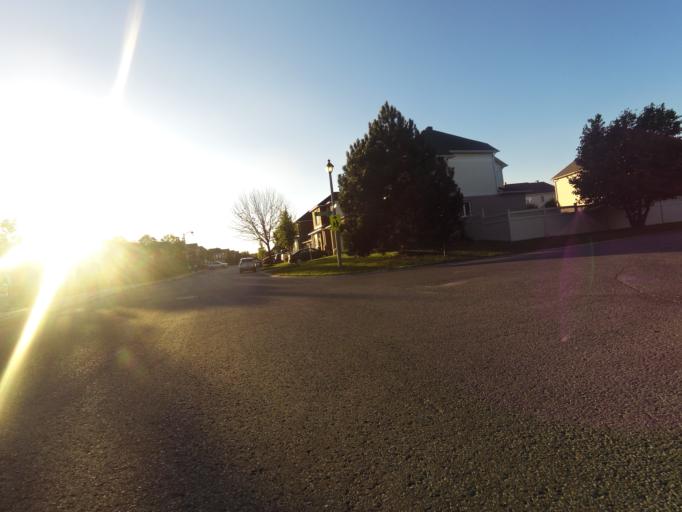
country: CA
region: Ontario
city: Bells Corners
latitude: 45.2783
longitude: -75.7091
